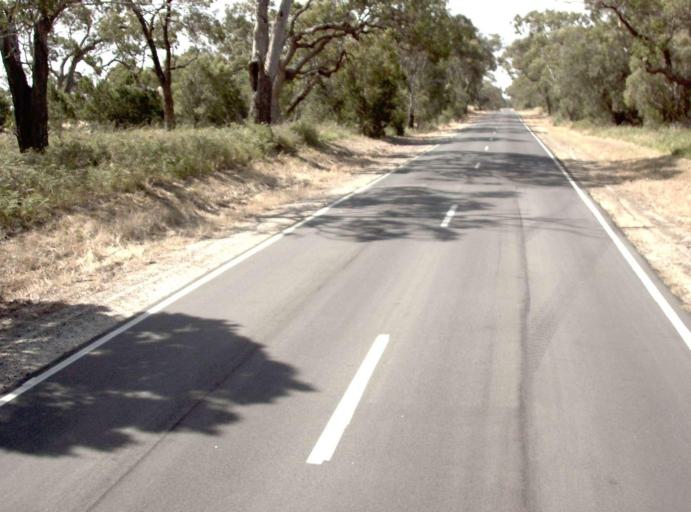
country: AU
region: Victoria
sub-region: Wellington
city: Sale
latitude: -38.3142
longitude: 147.1550
